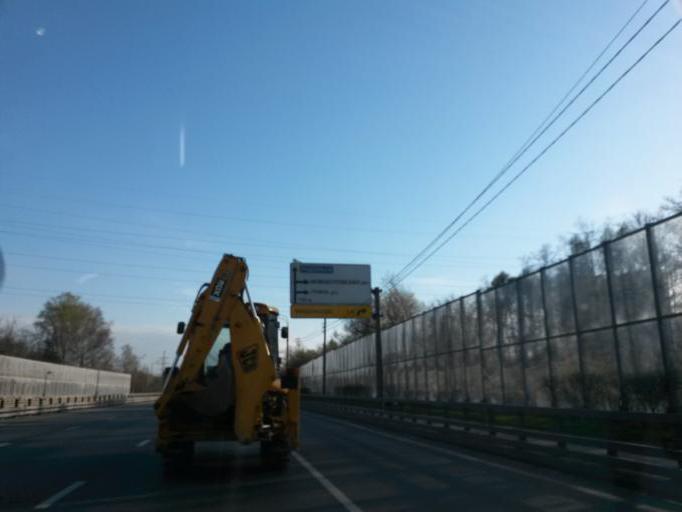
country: RU
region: Moscow
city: Annino
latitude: 55.5623
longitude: 37.5936
